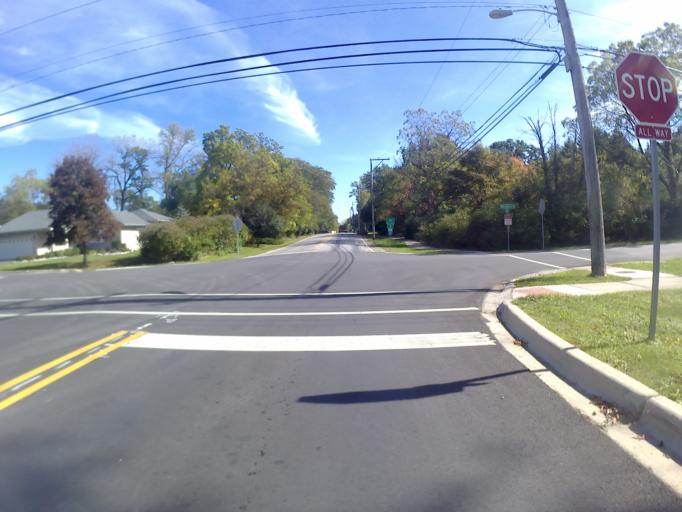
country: US
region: Illinois
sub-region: DuPage County
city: Clarendon Hills
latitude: 41.7812
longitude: -87.9629
